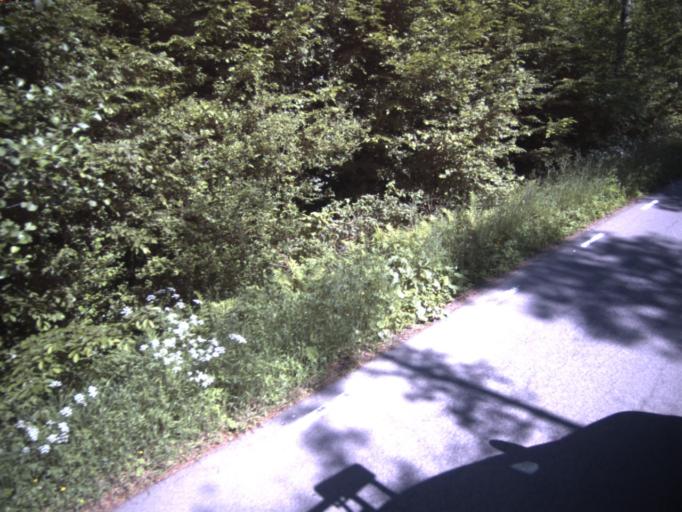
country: SE
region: Skane
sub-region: Helsingborg
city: Odakra
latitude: 56.1121
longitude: 12.6676
